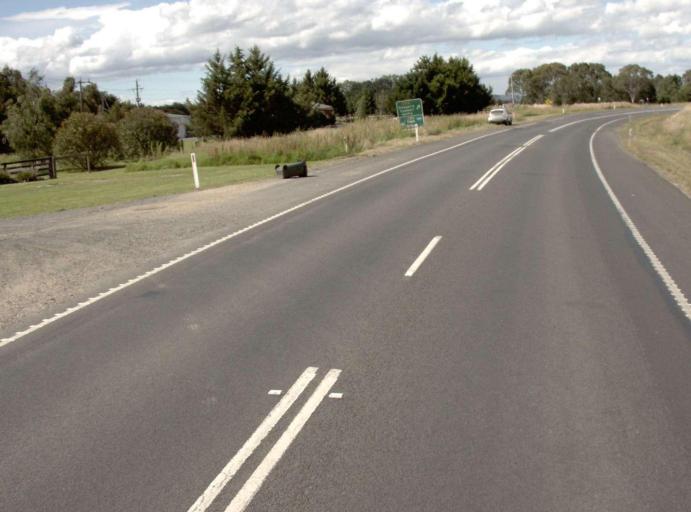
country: AU
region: Victoria
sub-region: Latrobe
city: Traralgon
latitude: -38.1327
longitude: 146.5586
